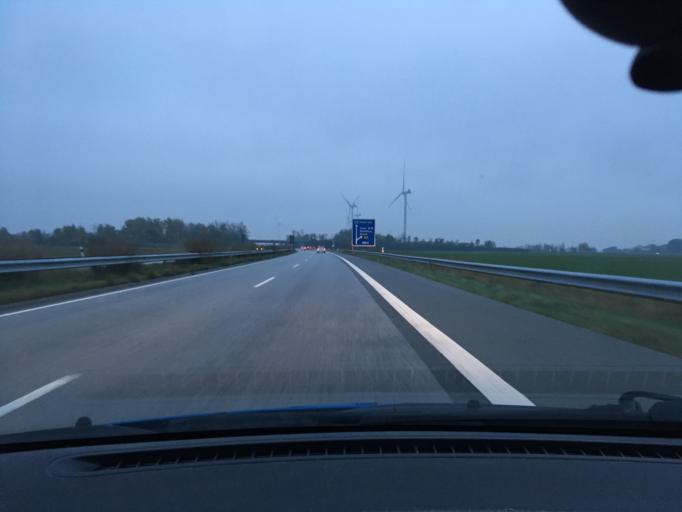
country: DE
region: Schleswig-Holstein
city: Lohe-Rickelshof
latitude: 54.1947
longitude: 9.0449
